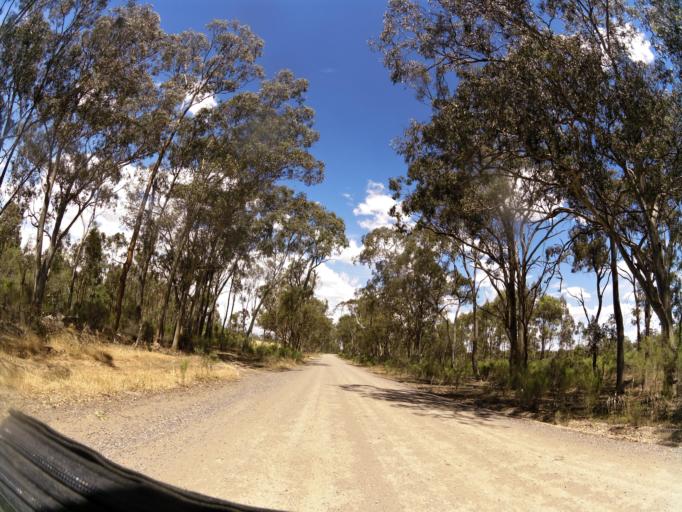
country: AU
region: Victoria
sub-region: Campaspe
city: Kyabram
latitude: -36.8113
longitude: 145.0755
